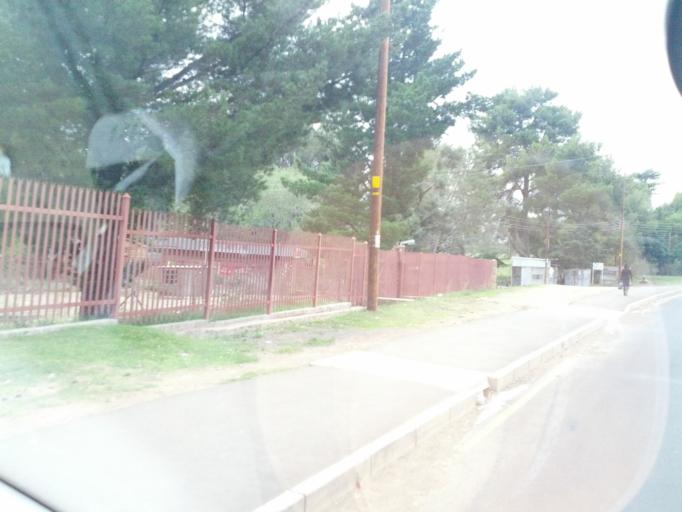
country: LS
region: Maseru
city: Nako
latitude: -29.4537
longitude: 27.7230
